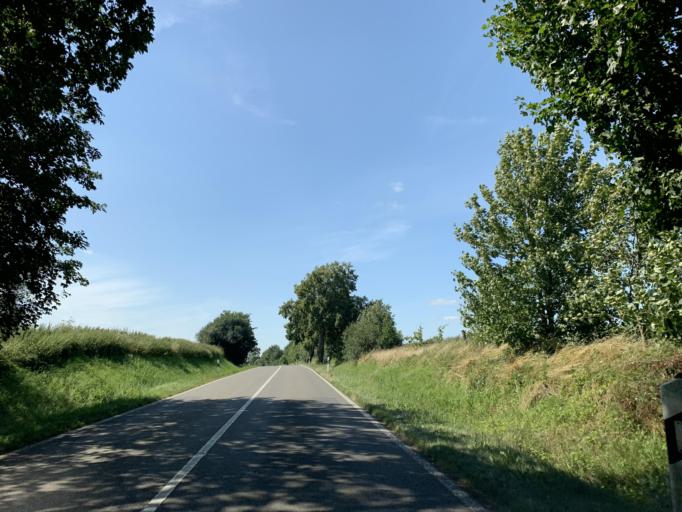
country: DE
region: Mecklenburg-Vorpommern
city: Blankensee
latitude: 53.3884
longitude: 13.3285
